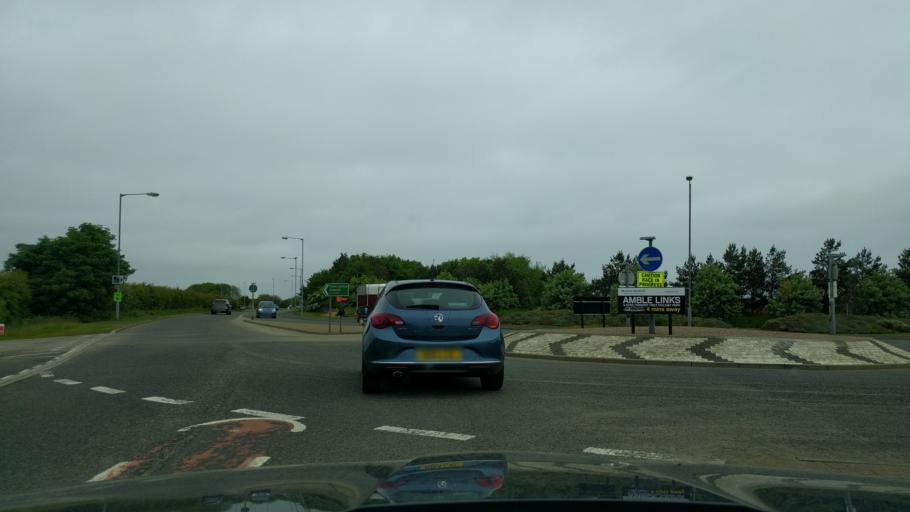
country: GB
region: England
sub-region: Northumberland
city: Amble
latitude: 55.3236
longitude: -1.5804
